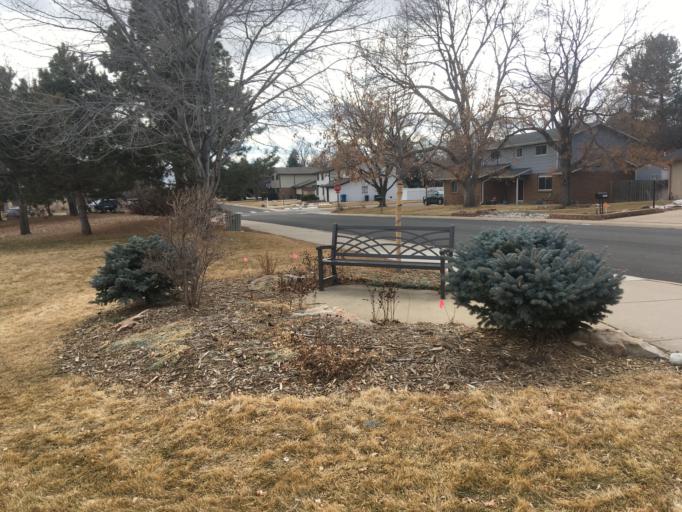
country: US
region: Colorado
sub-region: Broomfield County
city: Broomfield
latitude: 39.9368
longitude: -105.0592
